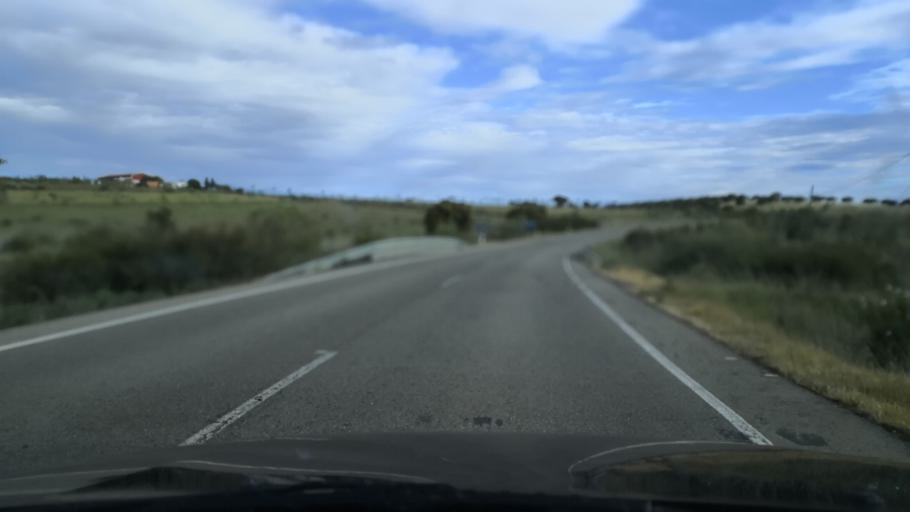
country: ES
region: Extremadura
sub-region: Provincia de Caceres
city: Perales del Puerto
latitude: 40.1170
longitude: -6.6706
